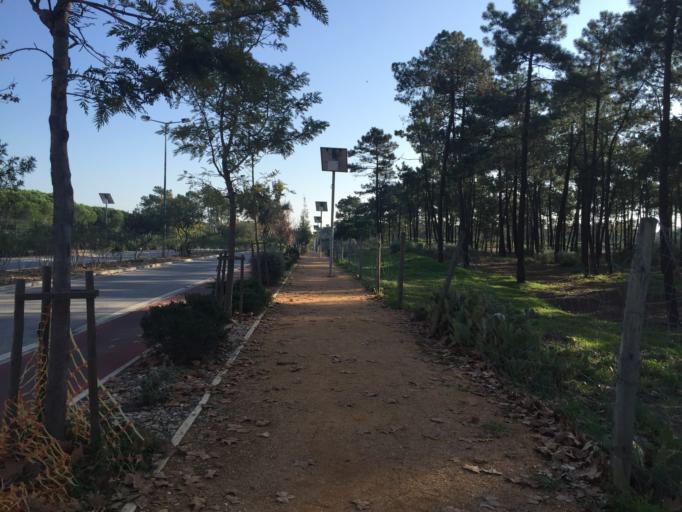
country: PT
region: Faro
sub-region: Vila Real de Santo Antonio
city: Vila Real de Santo Antonio
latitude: 37.1909
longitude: -7.4241
